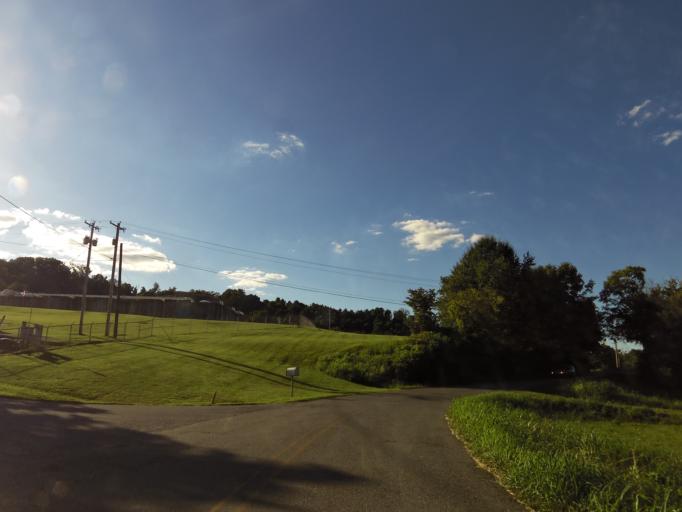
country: US
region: Tennessee
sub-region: Blount County
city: Eagleton Village
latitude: 35.8523
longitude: -83.9495
